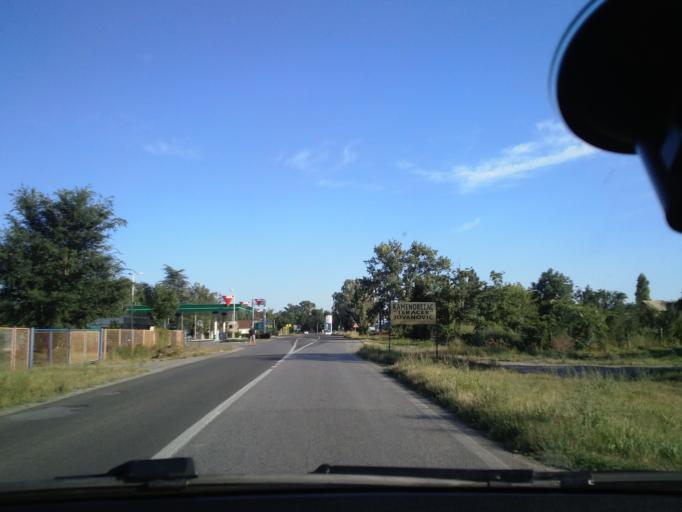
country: RS
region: Autonomna Pokrajina Vojvodina
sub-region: Zapadnobacki Okrug
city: Odzaci
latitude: 45.5171
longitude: 19.2471
